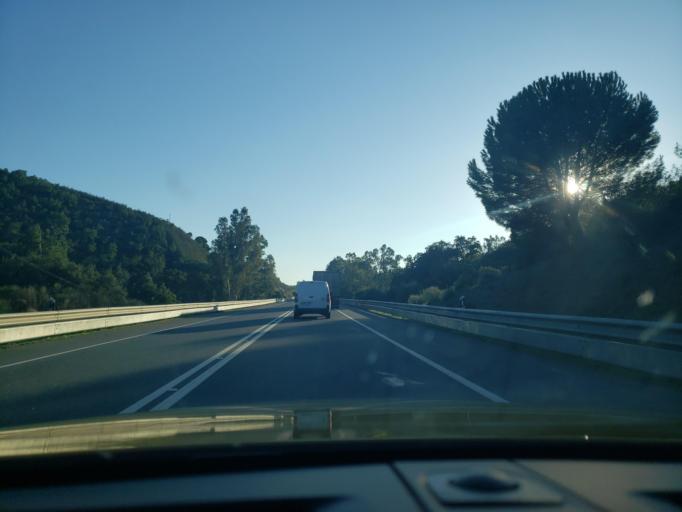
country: PT
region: Evora
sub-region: Portel
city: Portel
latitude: 38.3329
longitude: -7.6998
